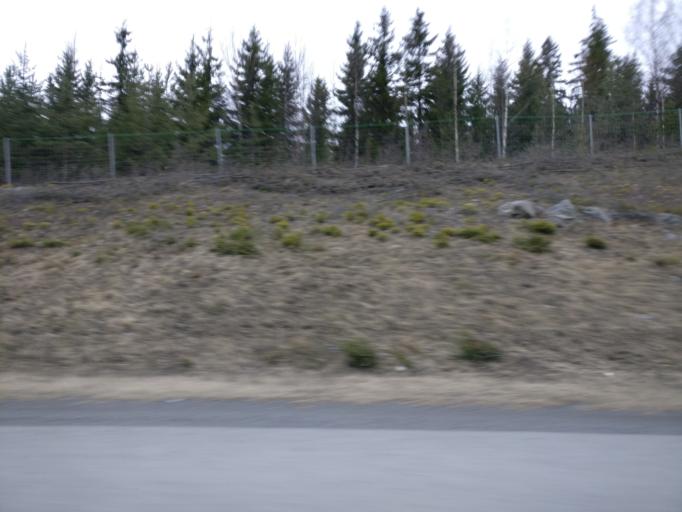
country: FI
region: Pirkanmaa
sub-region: Etelae-Pirkanmaa
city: Toijala
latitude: 61.2399
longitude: 23.8374
